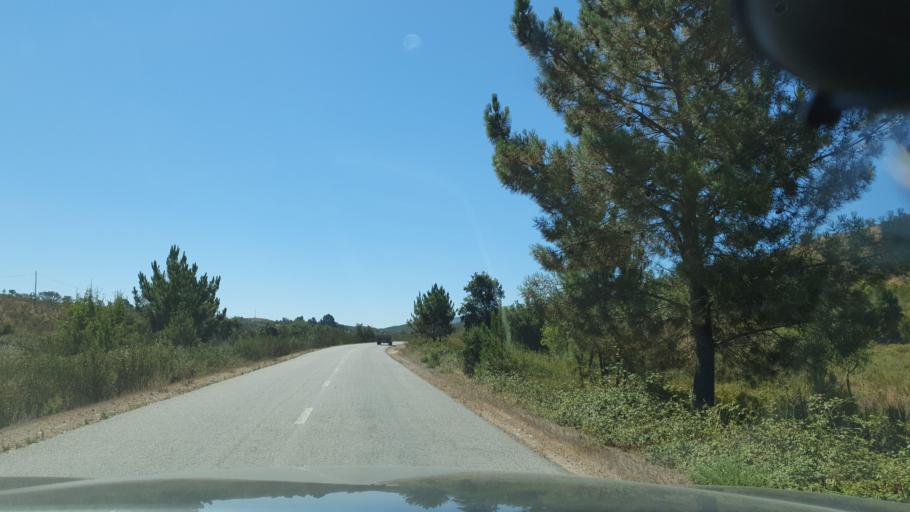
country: PT
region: Beja
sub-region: Odemira
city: Sao Teotonio
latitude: 37.4818
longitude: -8.6316
